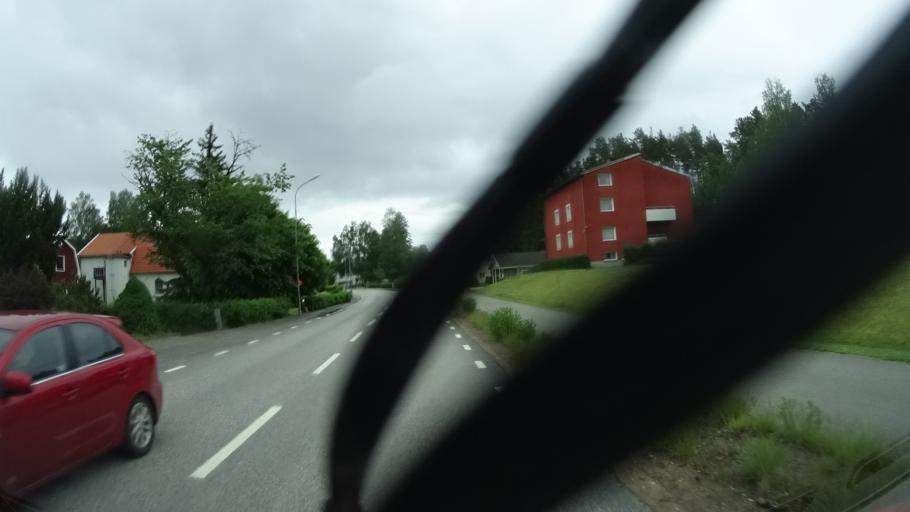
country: SE
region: Kalmar
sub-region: Hultsfreds Kommun
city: Hultsfred
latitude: 57.5438
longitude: 15.7465
